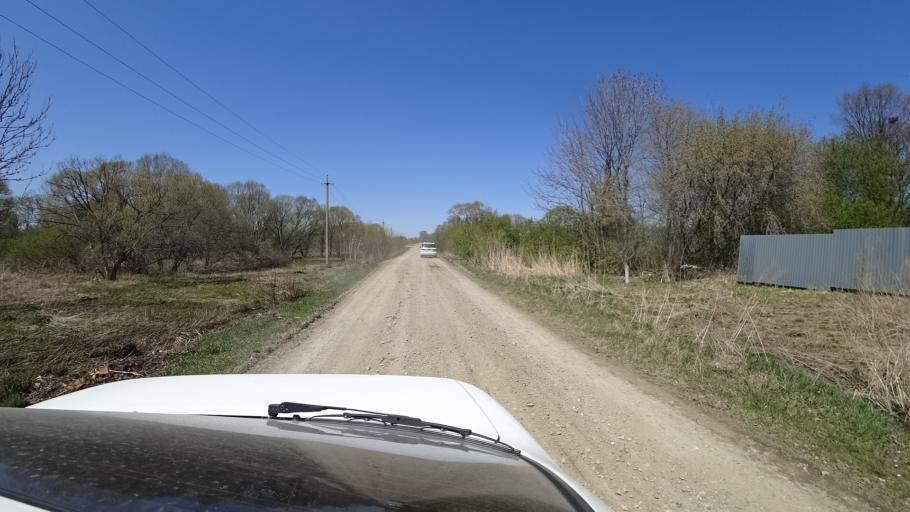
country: RU
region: Primorskiy
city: Lazo
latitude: 45.7943
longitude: 133.7633
